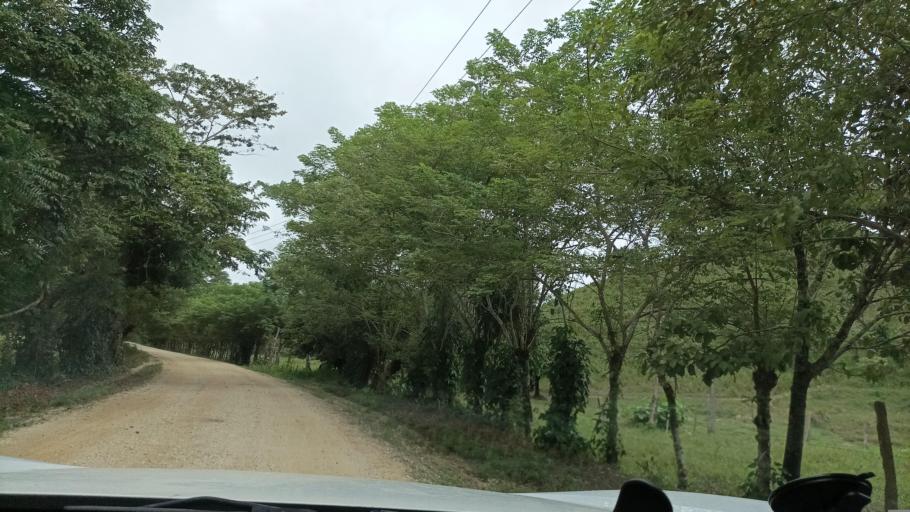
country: MX
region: Veracruz
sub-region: Moloacan
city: Cuichapa
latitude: 17.8366
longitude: -94.3543
